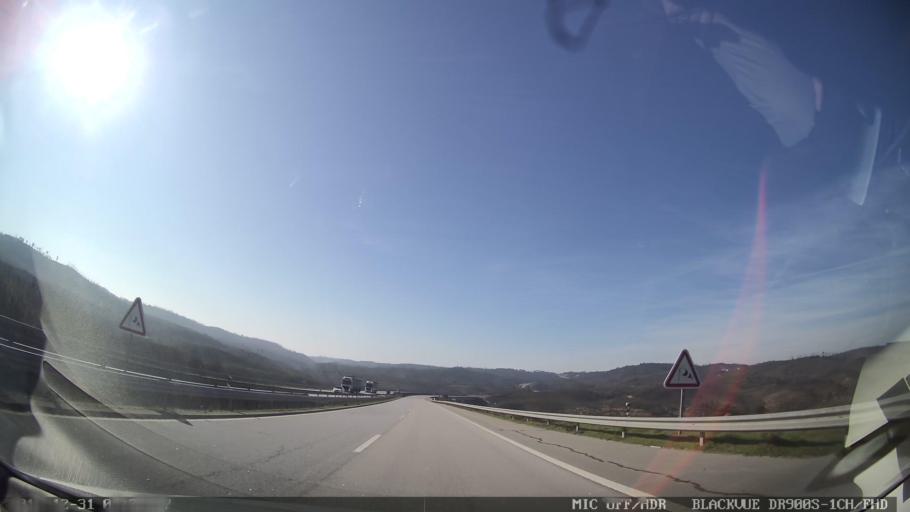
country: PT
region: Santarem
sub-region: Macao
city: Macao
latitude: 39.5238
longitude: -7.9737
